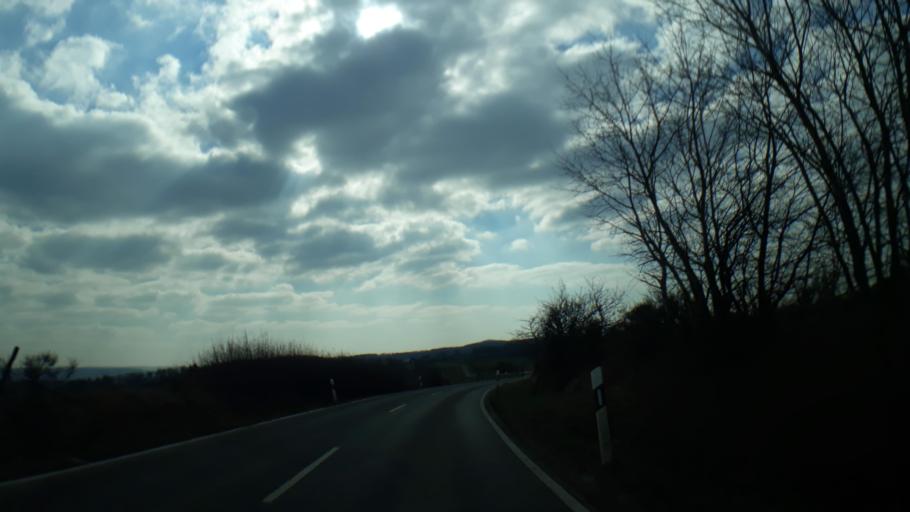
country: DE
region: Rheinland-Pfalz
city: Berg
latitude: 50.5663
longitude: 6.9466
